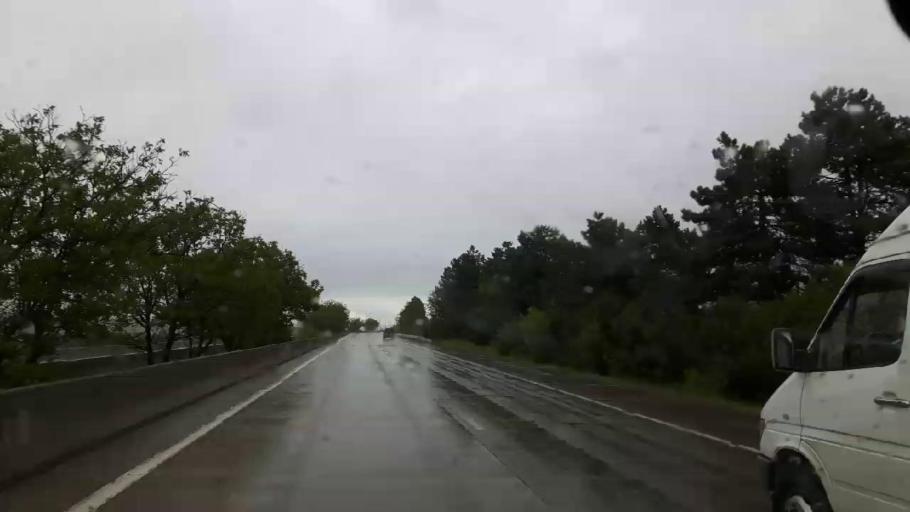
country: GE
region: Shida Kartli
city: Kaspi
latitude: 42.0226
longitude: 44.2849
